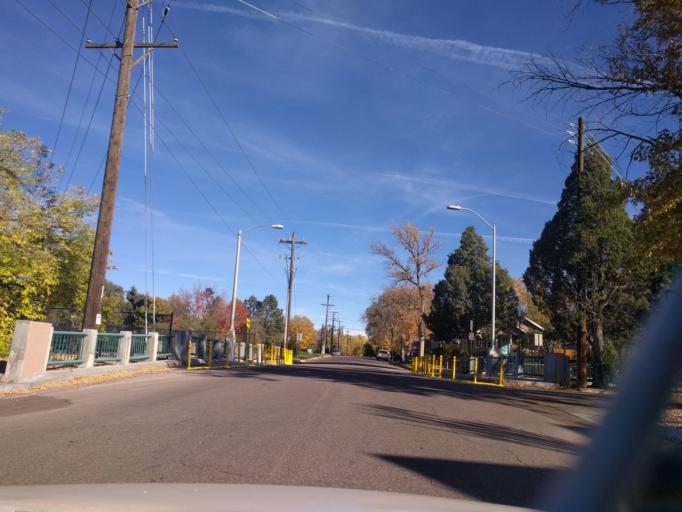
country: US
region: Colorado
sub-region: El Paso County
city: Colorado Springs
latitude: 38.8376
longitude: -104.8129
